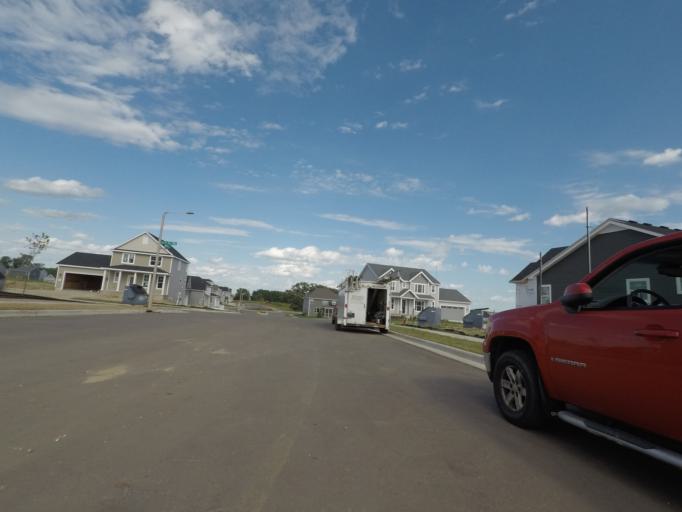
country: US
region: Wisconsin
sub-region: Dane County
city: Middleton
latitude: 43.0702
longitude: -89.5686
